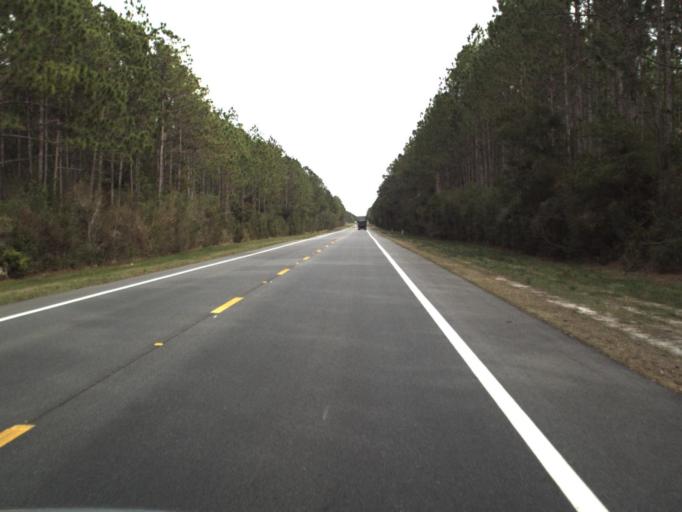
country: US
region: Florida
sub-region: Bay County
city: Callaway
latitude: 30.1526
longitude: -85.5137
